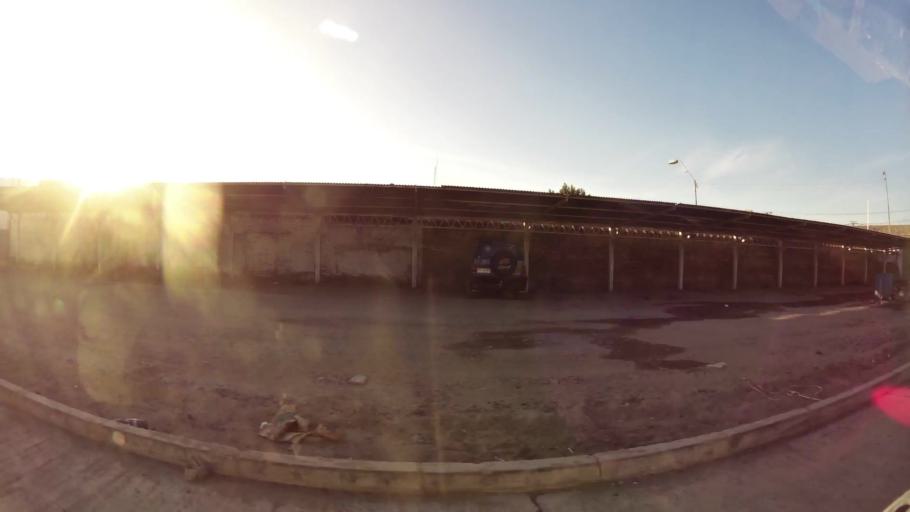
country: CL
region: Maule
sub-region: Provincia de Talca
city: Talca
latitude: -35.4348
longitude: -71.6426
